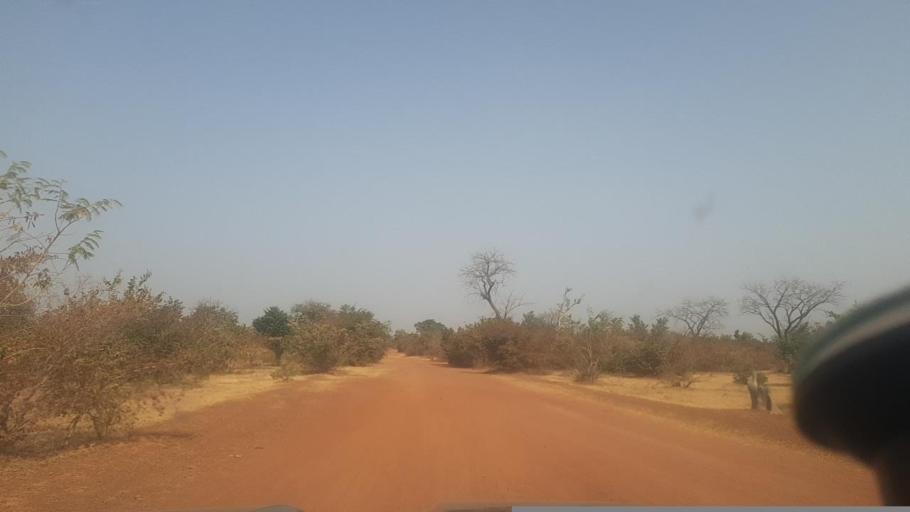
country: ML
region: Segou
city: Bla
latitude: 12.8584
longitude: -5.9694
